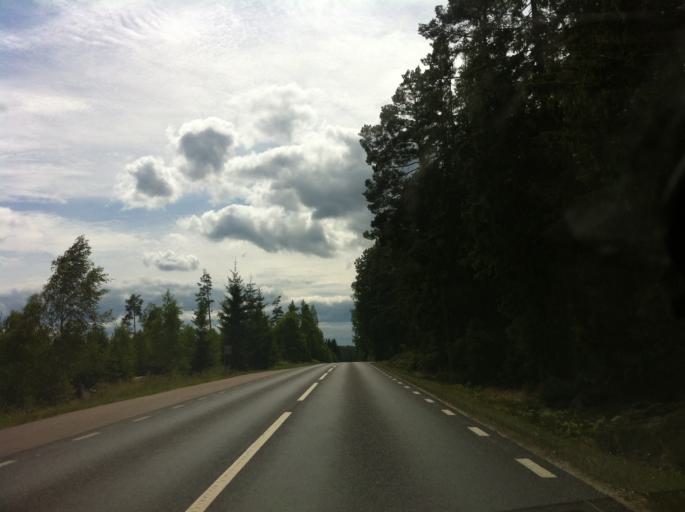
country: SE
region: Kalmar
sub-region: Emmaboda Kommun
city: Emmaboda
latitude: 56.6143
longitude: 15.4655
